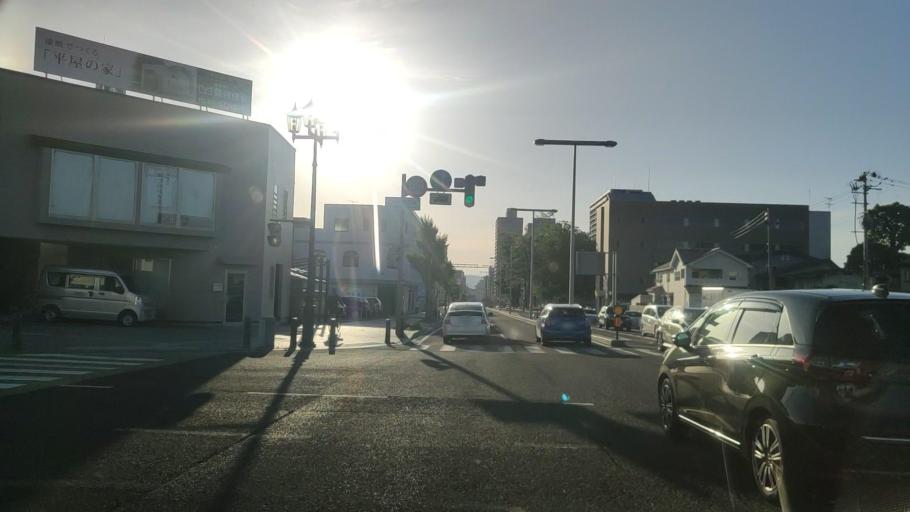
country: JP
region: Yamagata
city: Yamagata-shi
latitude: 38.2440
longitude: 140.3412
